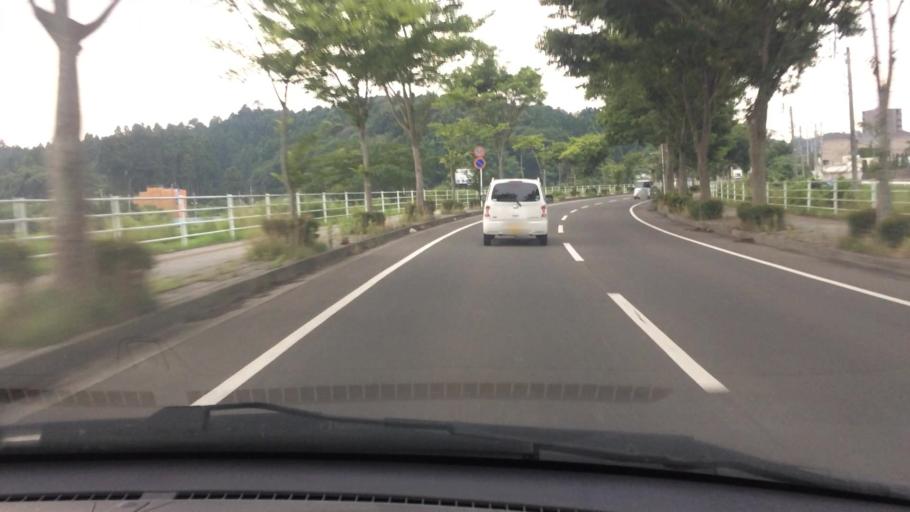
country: JP
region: Miyagi
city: Rifu
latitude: 38.3271
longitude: 140.9607
